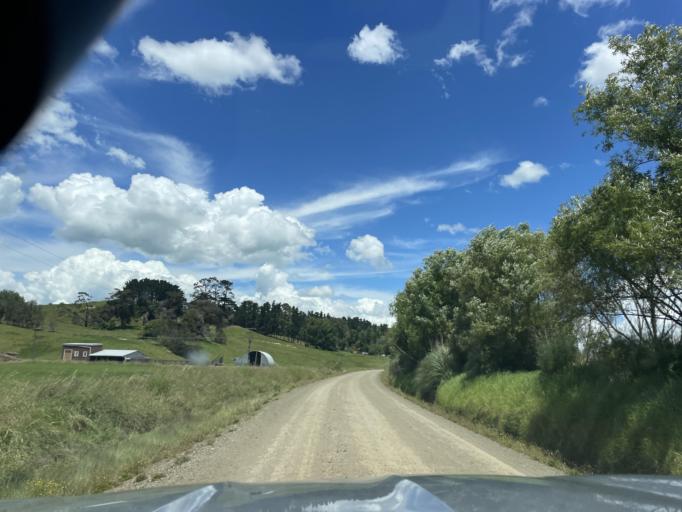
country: NZ
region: Northland
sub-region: Kaipara District
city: Dargaville
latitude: -35.9030
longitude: 173.9216
